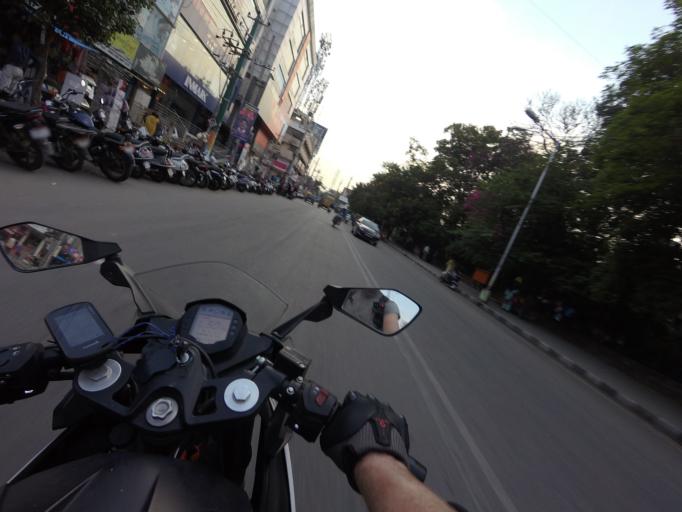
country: IN
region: Karnataka
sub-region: Bangalore Urban
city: Bangalore
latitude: 13.0219
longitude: 77.6371
